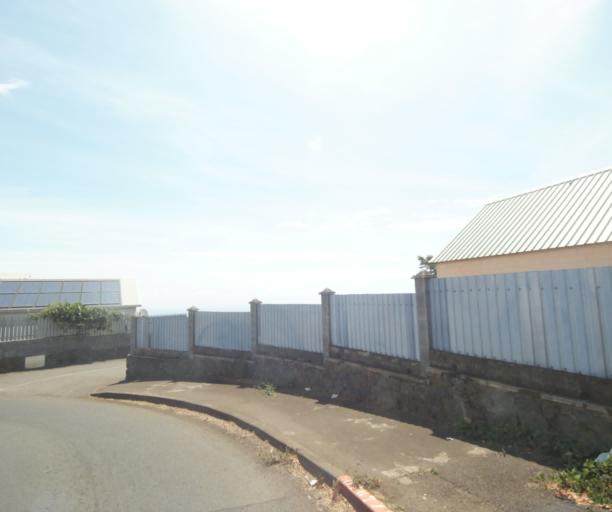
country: RE
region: Reunion
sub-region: Reunion
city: Trois-Bassins
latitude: -21.0987
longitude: 55.2732
